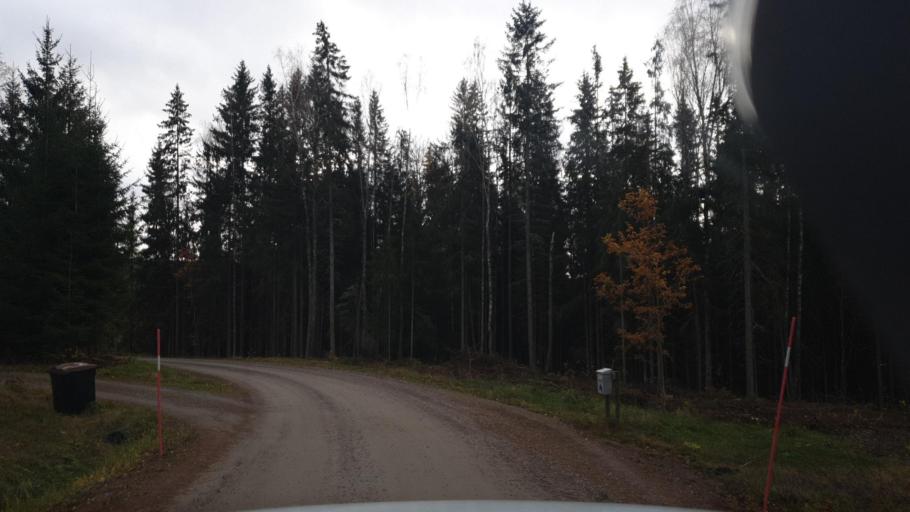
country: SE
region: Vaermland
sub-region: Arvika Kommun
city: Arvika
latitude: 59.5071
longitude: 12.7317
